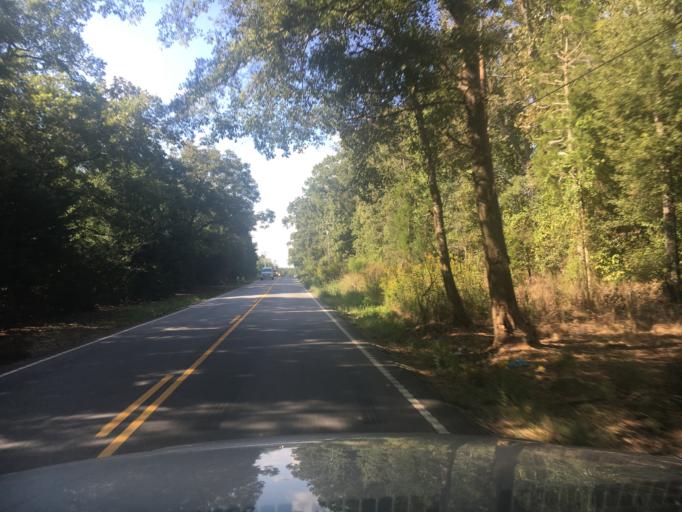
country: US
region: South Carolina
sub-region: Greenville County
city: Fountain Inn
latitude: 34.5981
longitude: -82.2280
